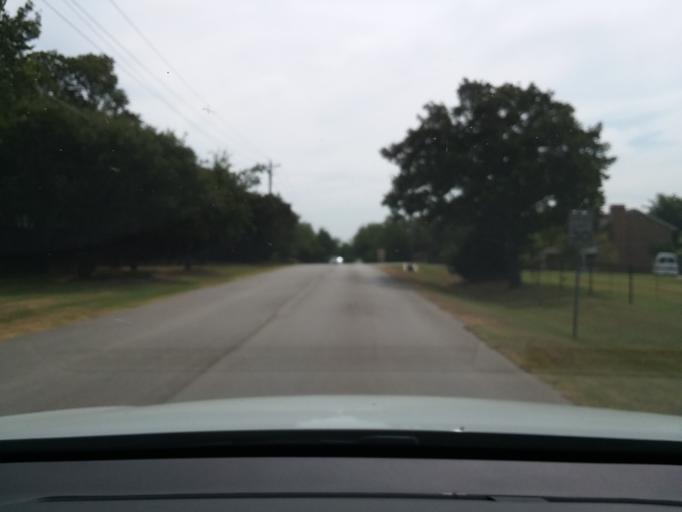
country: US
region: Texas
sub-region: Denton County
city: Double Oak
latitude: 33.0584
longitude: -97.1120
